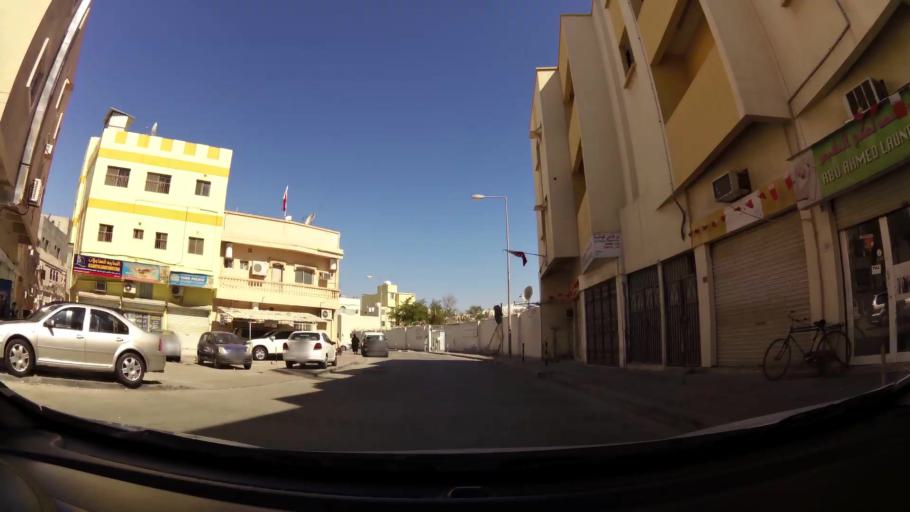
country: BH
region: Muharraq
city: Al Muharraq
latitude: 26.2467
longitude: 50.6180
